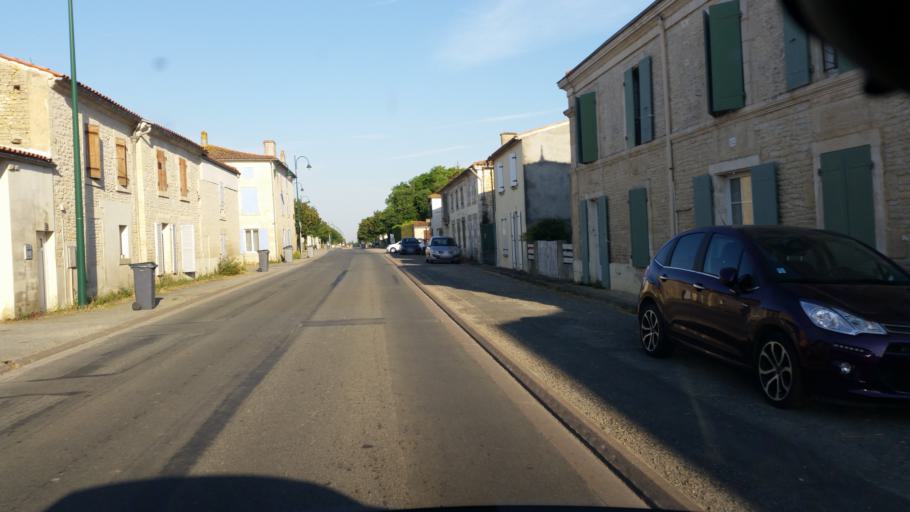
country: FR
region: Poitou-Charentes
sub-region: Departement de la Charente-Maritime
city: Saint-Jean-de-Liversay
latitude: 46.2273
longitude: -0.8603
